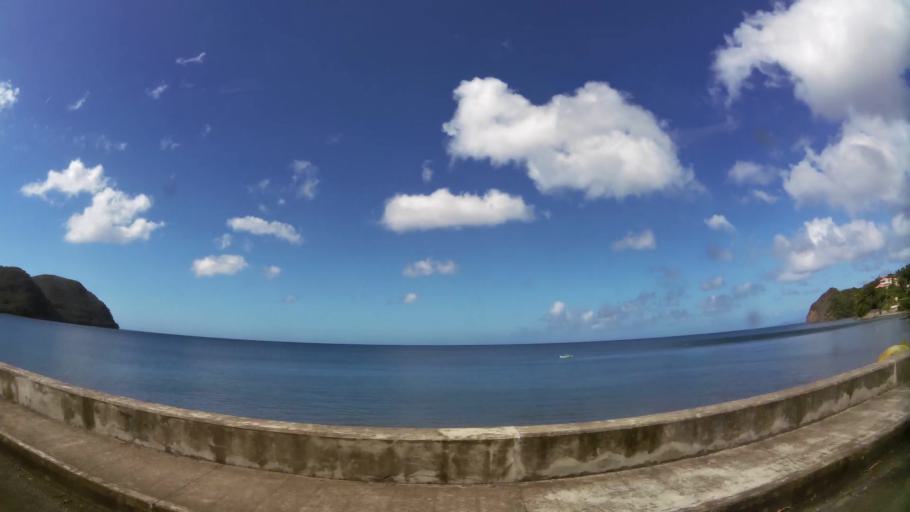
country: DM
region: Saint John
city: Portsmouth
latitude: 15.5986
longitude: -61.4616
